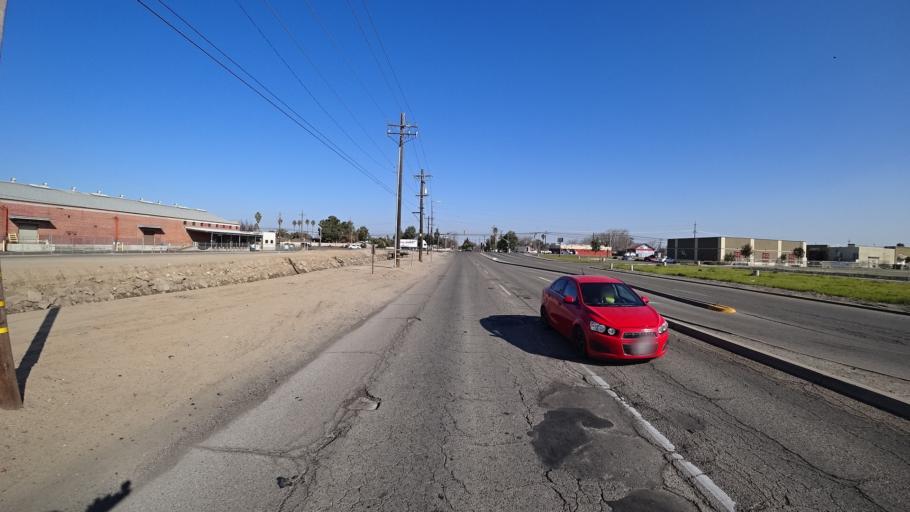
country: US
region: California
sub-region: Fresno County
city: Fresno
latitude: 36.7058
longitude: -119.7365
